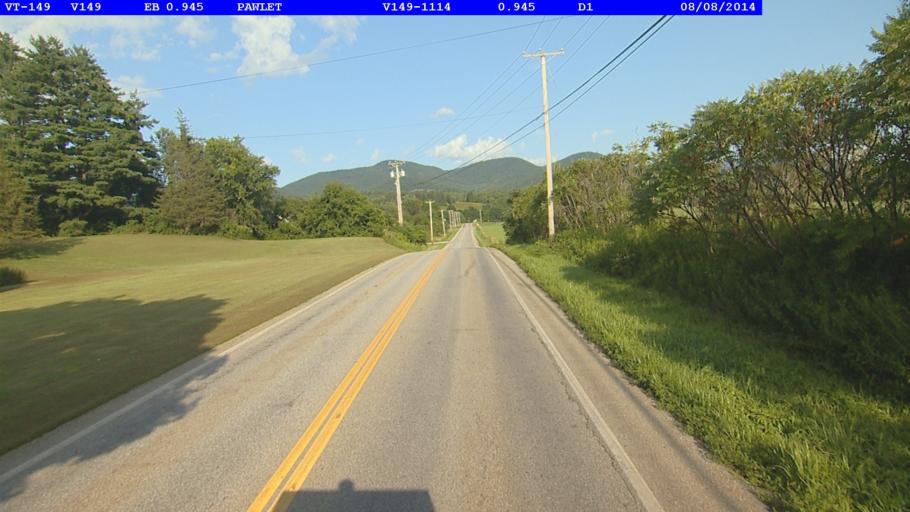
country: US
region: New York
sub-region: Washington County
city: Granville
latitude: 43.4024
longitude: -73.2330
